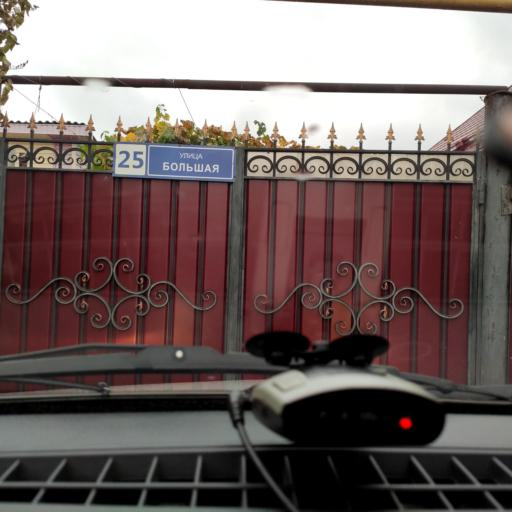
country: RU
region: Voronezj
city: Pridonskoy
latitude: 51.7034
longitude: 39.0694
